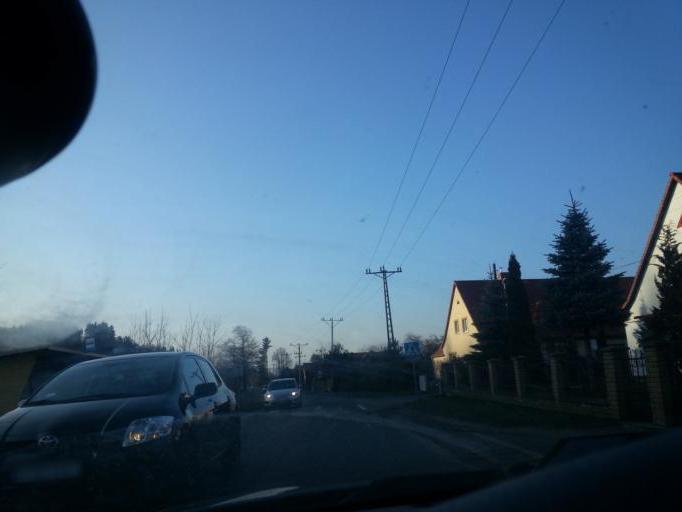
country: PL
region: Lower Silesian Voivodeship
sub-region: Powiat jeleniogorski
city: Myslakowice
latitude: 50.8875
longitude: 15.7940
